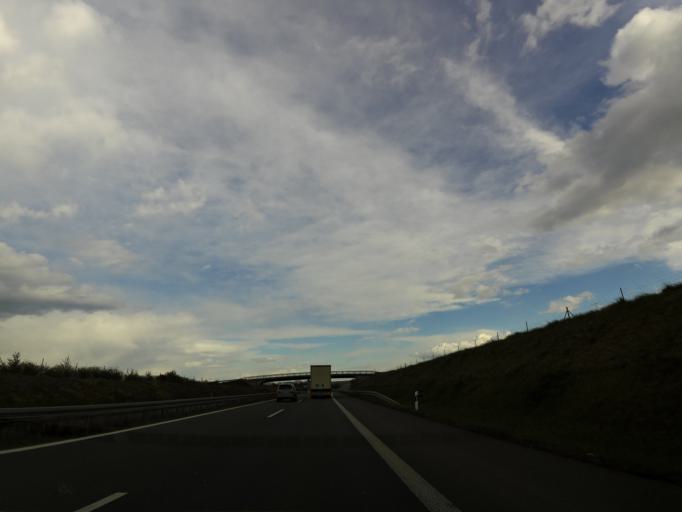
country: DE
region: Saxony-Anhalt
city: Quedlinburg
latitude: 51.8135
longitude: 11.1690
